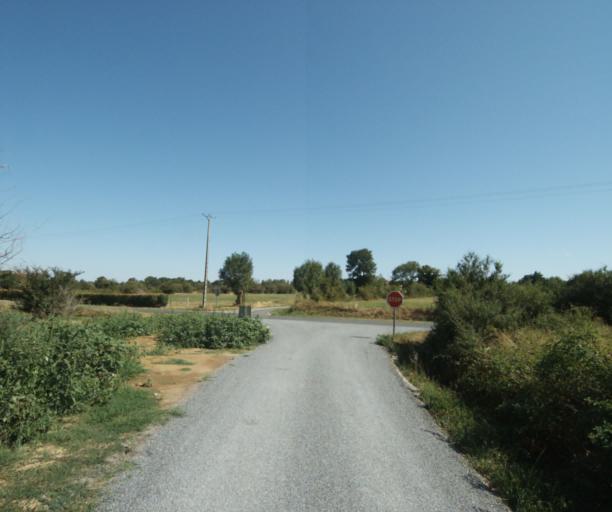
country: FR
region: Midi-Pyrenees
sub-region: Departement du Tarn
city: Soreze
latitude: 43.4447
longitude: 2.0567
